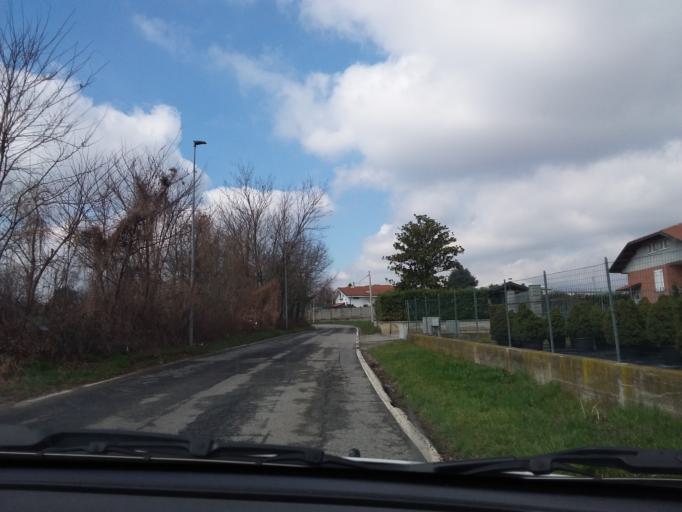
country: IT
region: Piedmont
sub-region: Provincia di Torino
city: Tetti Neirotti
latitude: 45.0555
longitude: 7.5339
